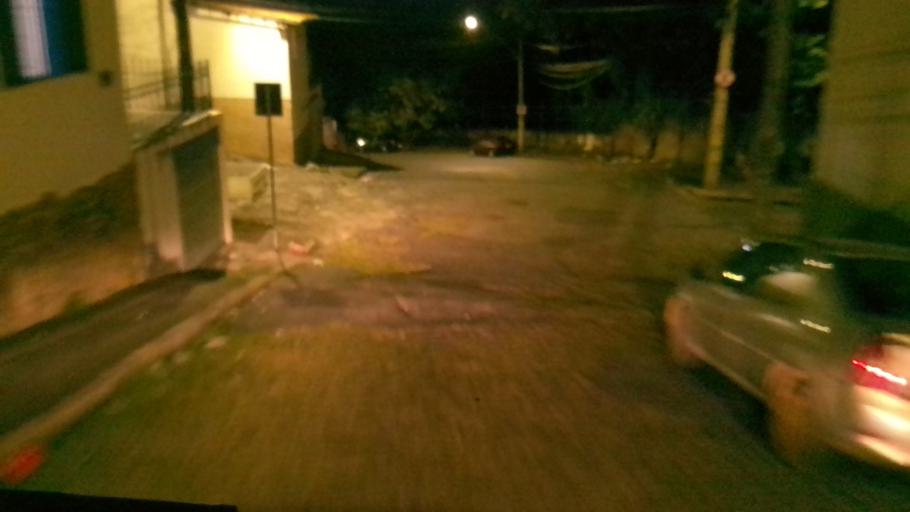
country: BR
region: Minas Gerais
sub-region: Belo Horizonte
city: Belo Horizonte
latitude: -19.9194
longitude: -43.9246
